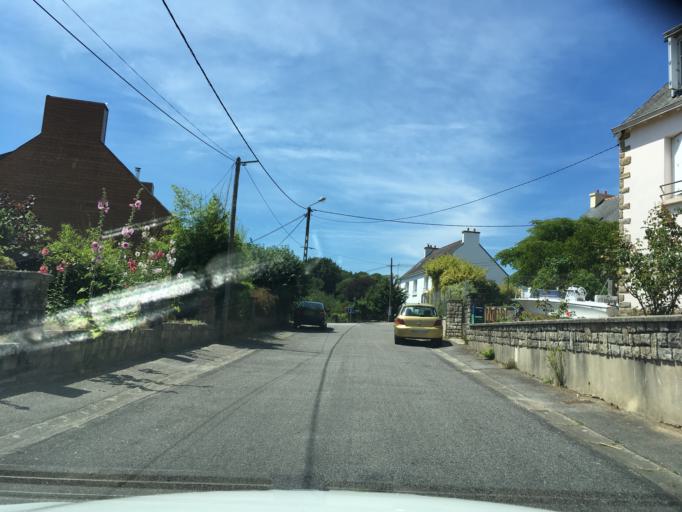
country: FR
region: Brittany
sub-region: Departement du Finistere
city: Quimper
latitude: 47.9968
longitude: -4.1289
